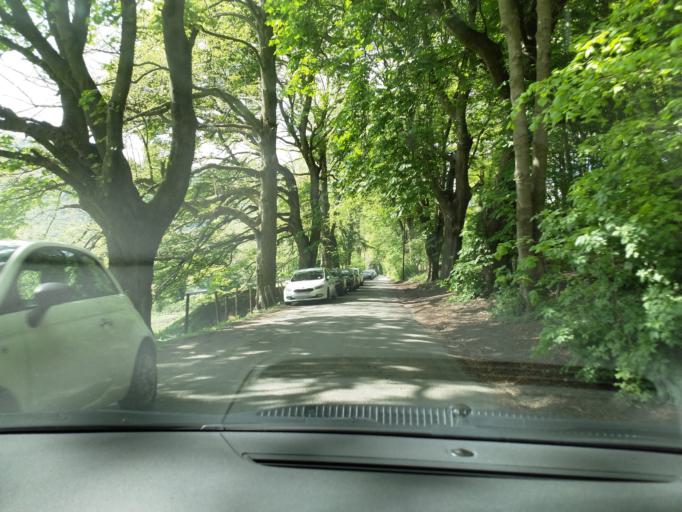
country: GB
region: England
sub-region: Derbyshire
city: Hope Valley
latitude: 53.3587
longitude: -1.6957
